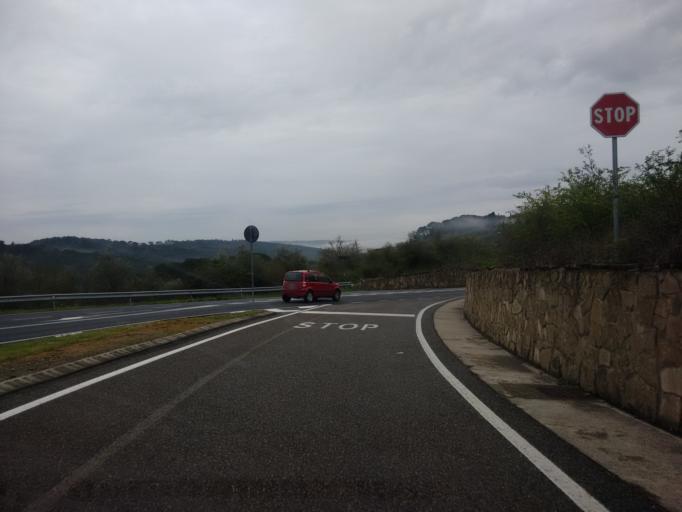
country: IT
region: Tuscany
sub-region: Province of Florence
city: Strada in Chianti
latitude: 43.6544
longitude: 11.3006
